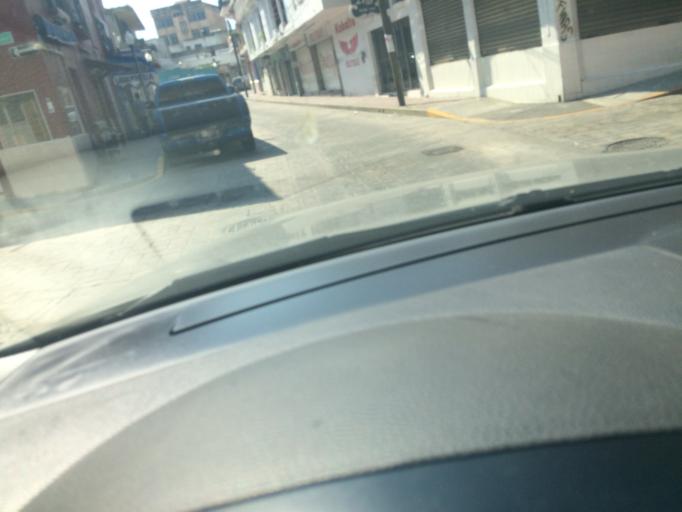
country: MX
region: Colima
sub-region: Manzanillo
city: Manzanillo
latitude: 19.0534
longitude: -104.3178
